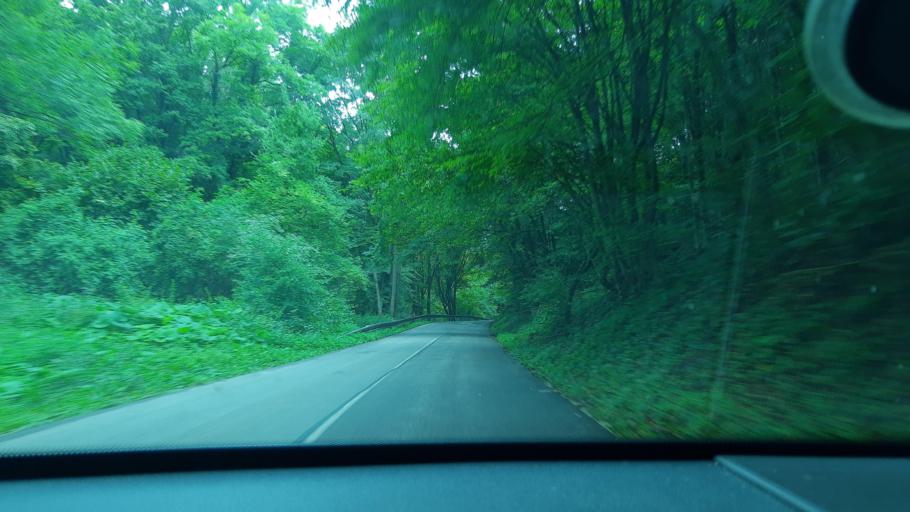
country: SK
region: Trnavsky
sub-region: Okres Trnava
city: Piestany
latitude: 48.6432
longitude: 17.9364
